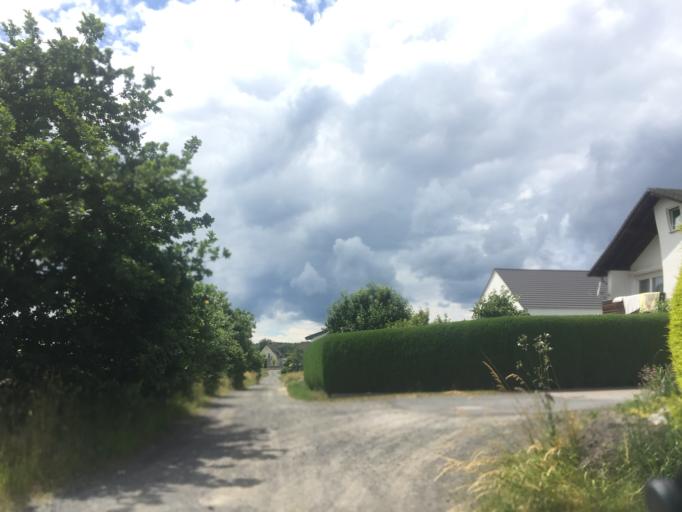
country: DE
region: Rheinland-Pfalz
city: Girod
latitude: 50.4501
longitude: 7.9127
